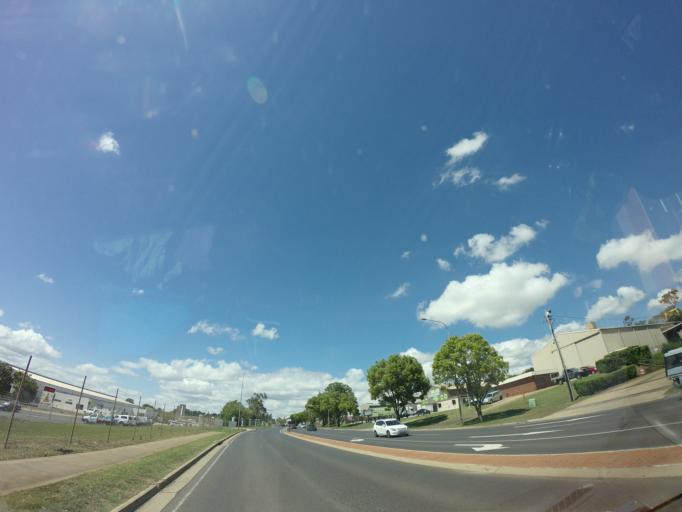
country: AU
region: Queensland
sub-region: Toowoomba
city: Darling Heights
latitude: -27.5854
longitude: 151.9175
